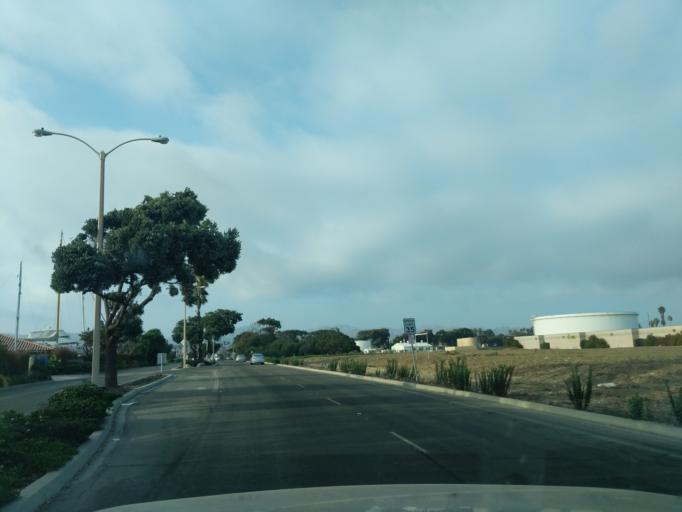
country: US
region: California
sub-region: Ventura County
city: Ventura
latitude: 34.2403
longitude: -119.2611
